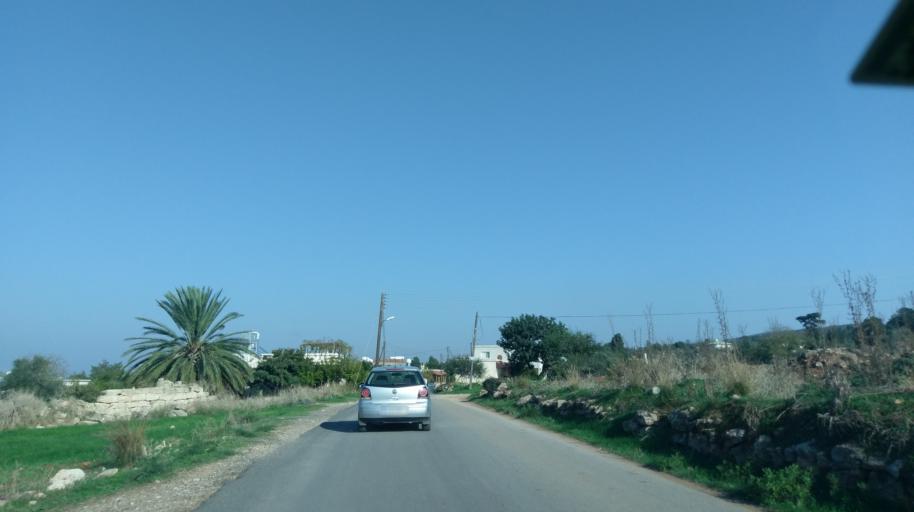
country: CY
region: Ammochostos
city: Leonarisso
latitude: 35.5345
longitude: 34.1926
